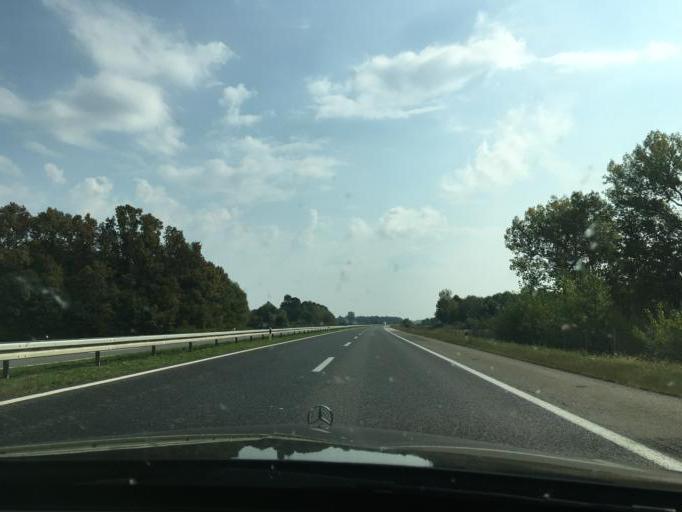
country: HR
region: Brodsko-Posavska
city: Garcin
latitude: 45.1547
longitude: 18.2448
